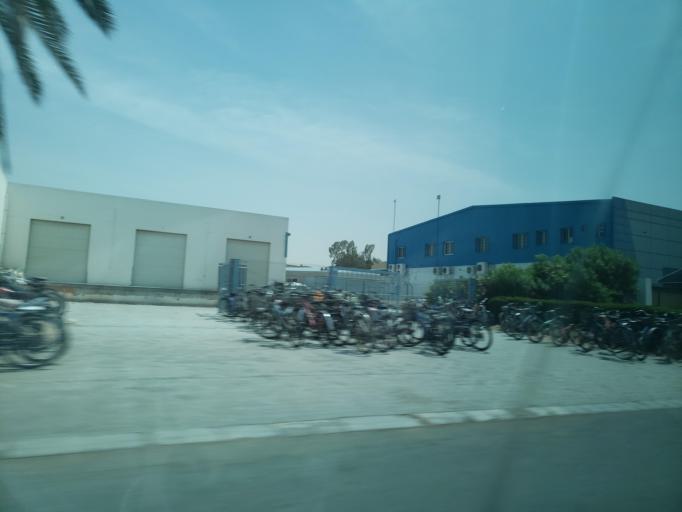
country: AE
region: Ash Shariqah
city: Sharjah
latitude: 25.3307
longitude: 55.4945
